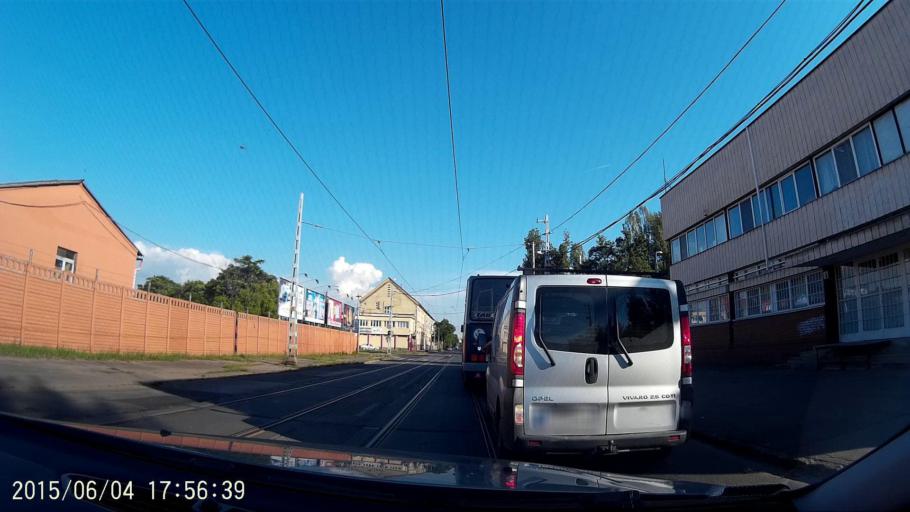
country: HU
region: Budapest
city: Budapest XX. keruelet
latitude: 47.4545
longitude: 19.0907
